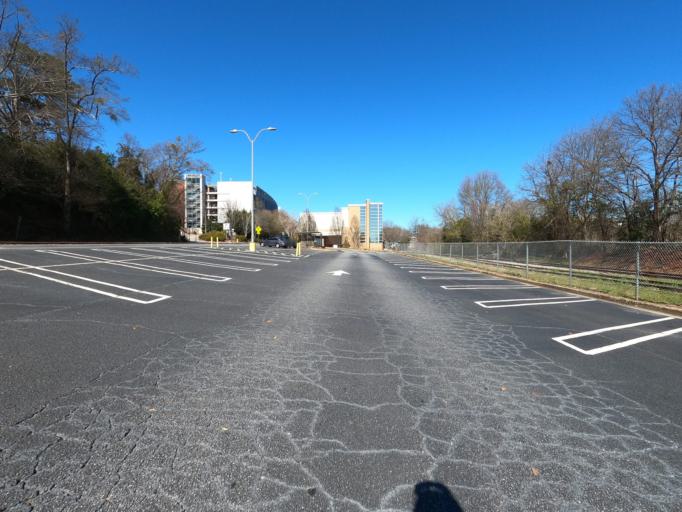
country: US
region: Georgia
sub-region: Clarke County
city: Athens
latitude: 33.9545
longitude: -83.3713
